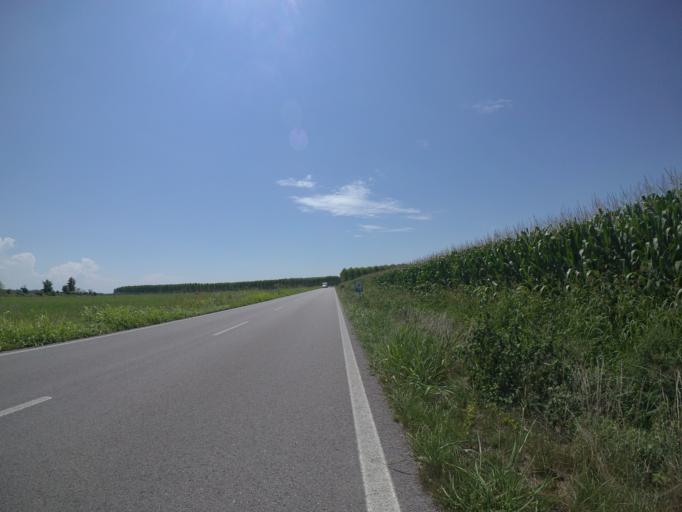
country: IT
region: Friuli Venezia Giulia
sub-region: Provincia di Udine
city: Talmassons
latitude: 45.9045
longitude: 13.1356
